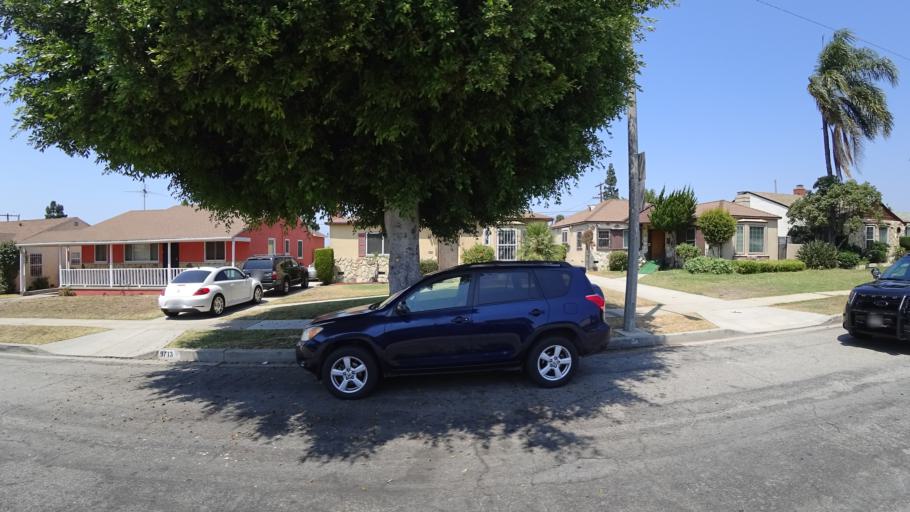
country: US
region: California
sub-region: Los Angeles County
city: Westmont
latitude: 33.9475
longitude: -118.3254
